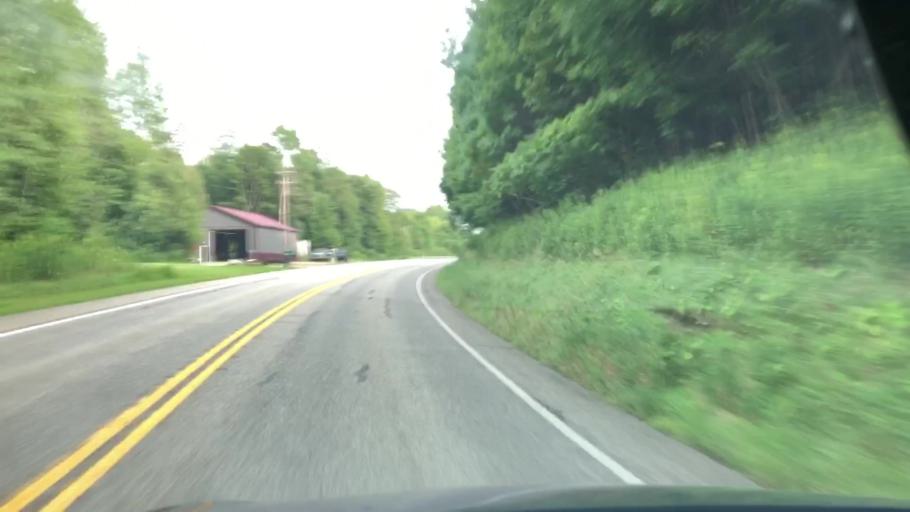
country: US
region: Pennsylvania
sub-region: Erie County
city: Union City
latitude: 42.0506
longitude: -79.8460
